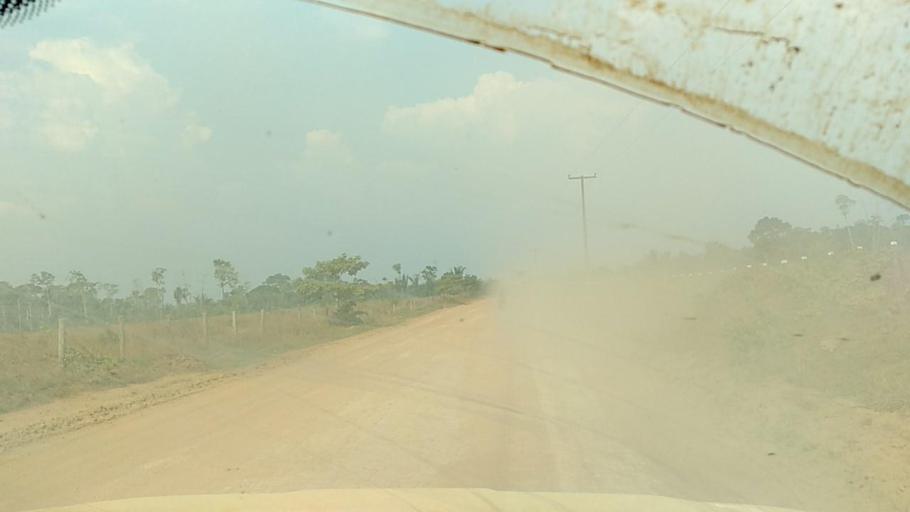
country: BR
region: Rondonia
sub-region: Porto Velho
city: Porto Velho
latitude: -8.6831
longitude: -63.2004
